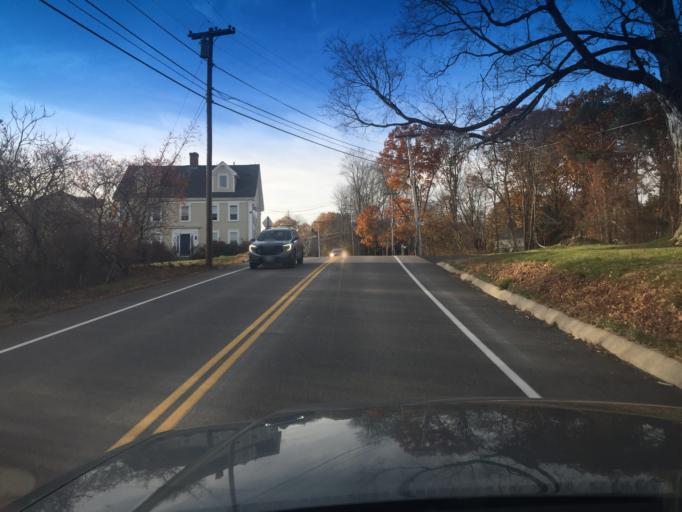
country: US
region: Maine
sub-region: York County
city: York Harbor
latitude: 43.1587
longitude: -70.6981
